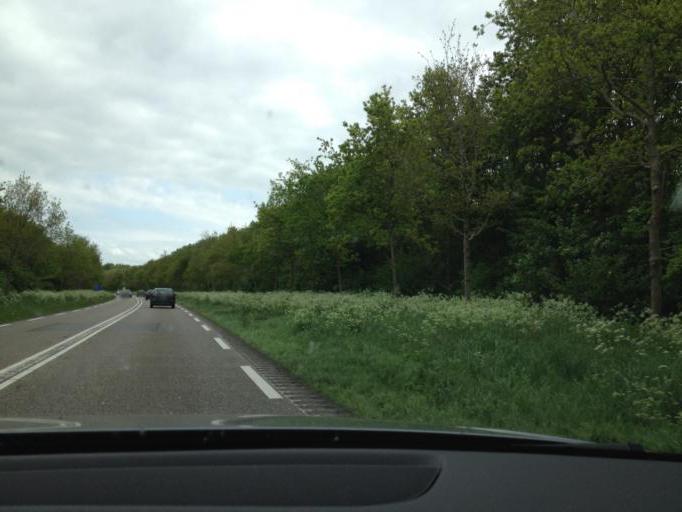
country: NL
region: North Holland
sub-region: Gemeente Huizen
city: Huizen
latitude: 52.3450
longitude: 5.2624
